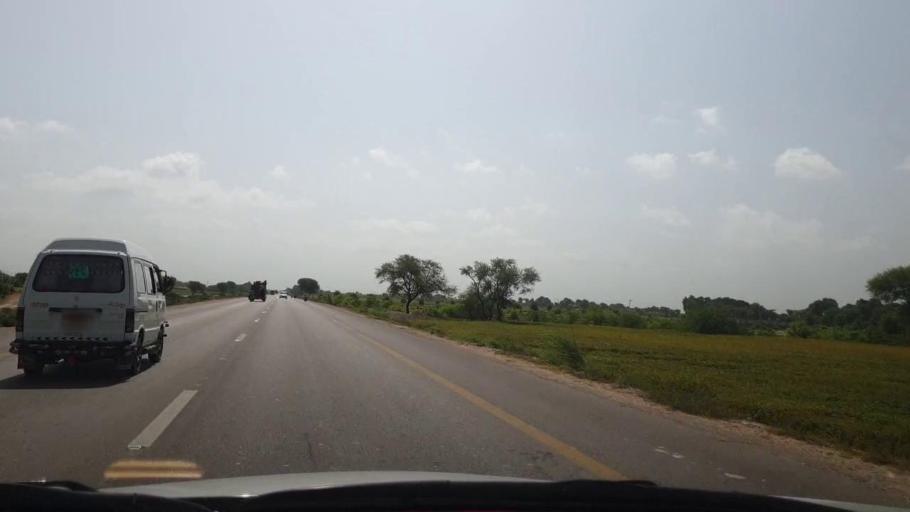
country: PK
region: Sindh
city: Matli
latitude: 24.9821
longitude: 68.6649
